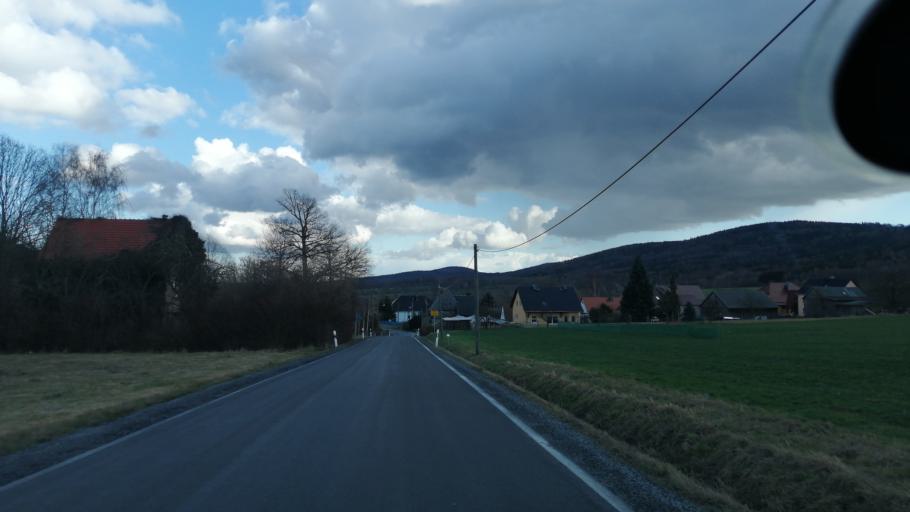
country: DE
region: Saxony
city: Kubschutz
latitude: 51.1364
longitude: 14.4927
